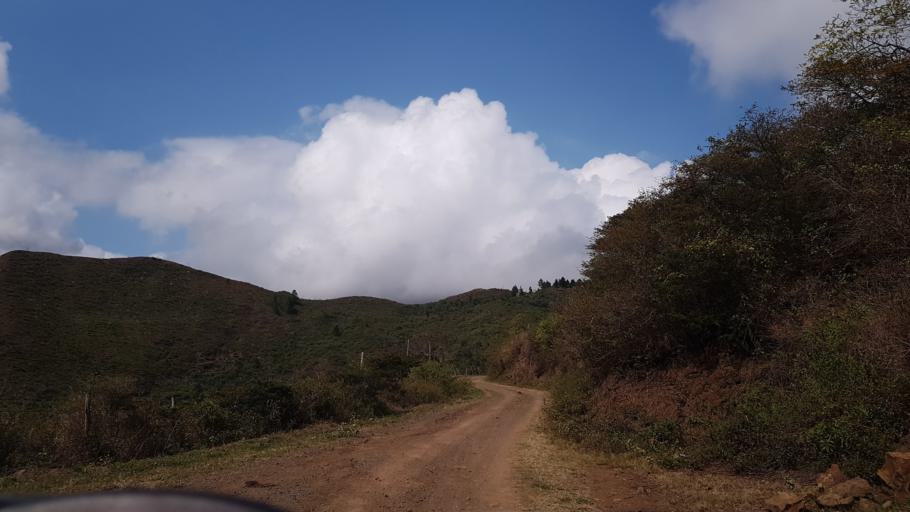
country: CO
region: Valle del Cauca
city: Yumbo
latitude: 3.6526
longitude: -76.5137
